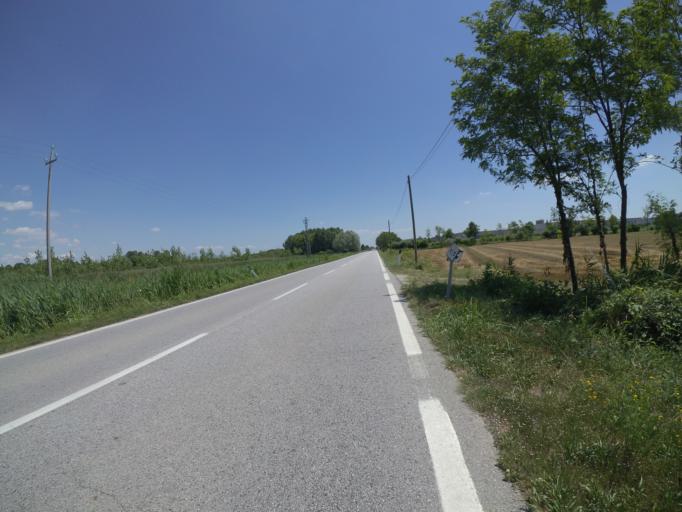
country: IT
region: Friuli Venezia Giulia
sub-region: Provincia di Udine
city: Rivignano
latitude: 45.8810
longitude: 13.0221
